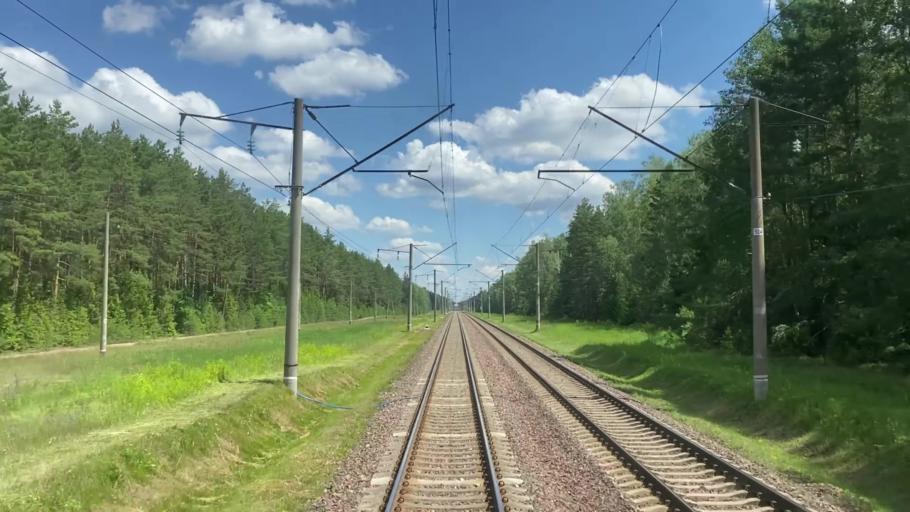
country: BY
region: Grodnenskaya
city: Zhyrovichy
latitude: 52.8635
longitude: 25.5930
